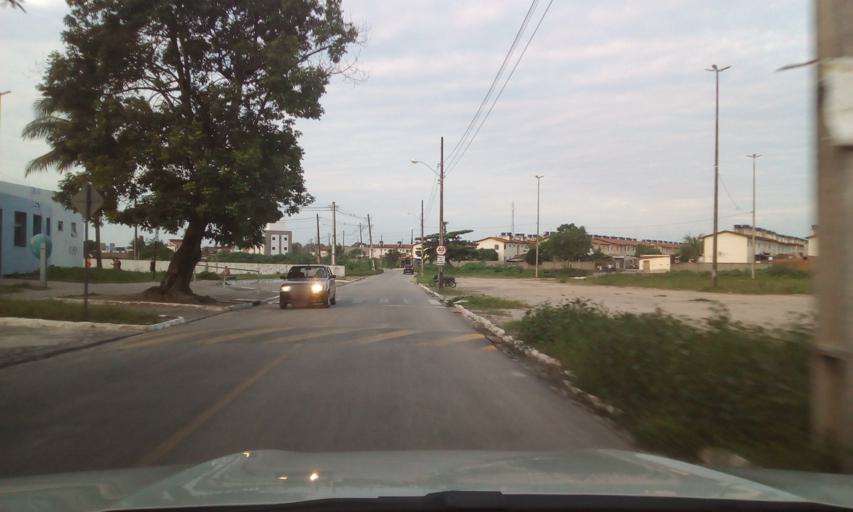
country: BR
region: Paraiba
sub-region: Conde
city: Conde
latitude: -7.2099
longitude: -34.8397
